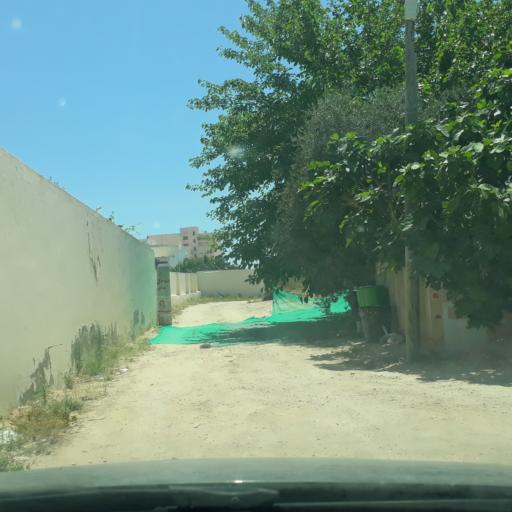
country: TN
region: Safaqis
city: Al Qarmadah
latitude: 34.8109
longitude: 10.7592
